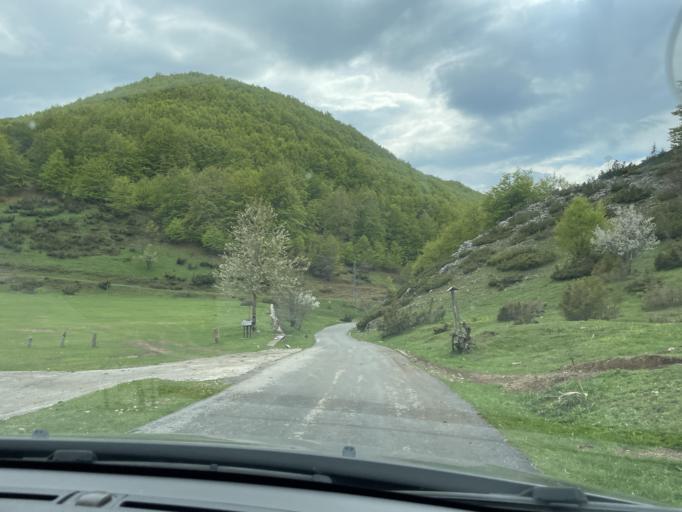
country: MK
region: Opstina Rostusa
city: Rostusha
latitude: 41.5949
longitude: 20.6726
